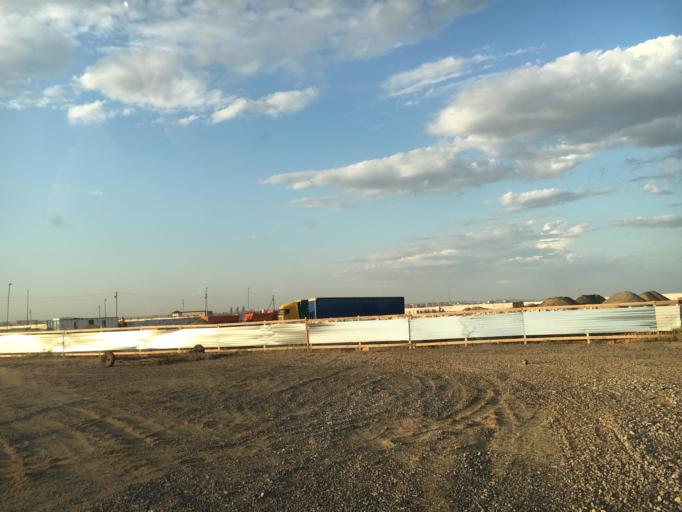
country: KZ
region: Aqtoebe
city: Aqtobe
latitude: 50.2335
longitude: 57.1723
